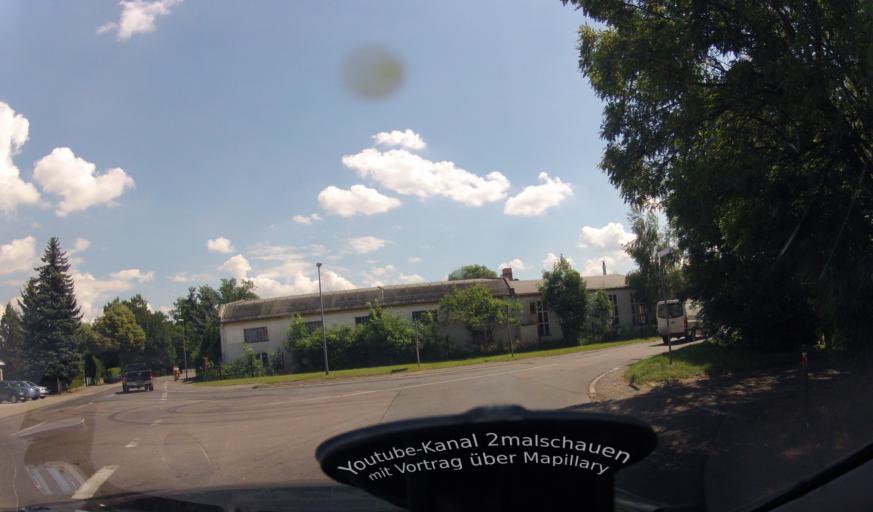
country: DE
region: Saxony
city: Torgau
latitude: 51.5655
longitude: 12.9981
